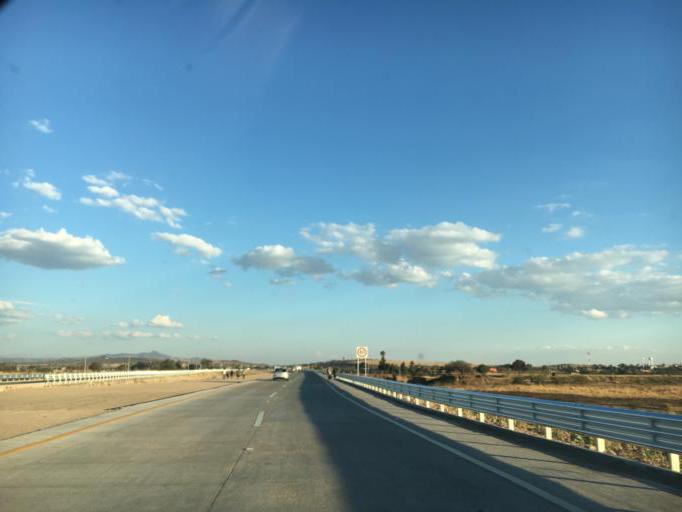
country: MX
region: Guanajuato
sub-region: Leon
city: Ladrilleras del Refugio
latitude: 21.0815
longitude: -101.5518
